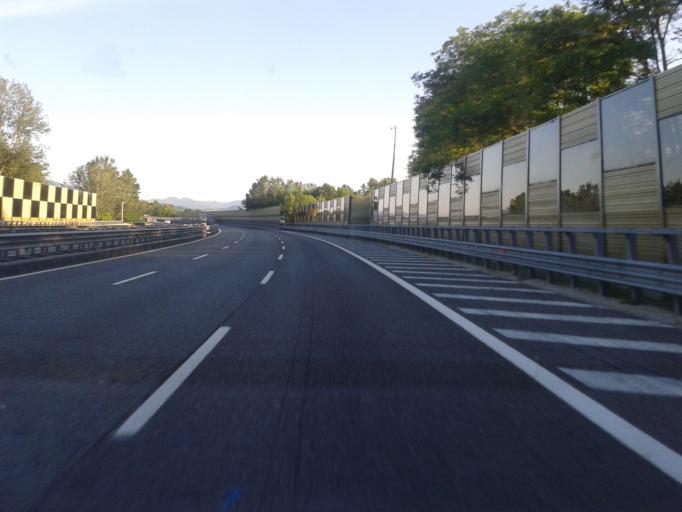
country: IT
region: Piedmont
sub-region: Provincia di Alessandria
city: Rocca Grimalda
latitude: 44.6771
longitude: 8.6581
